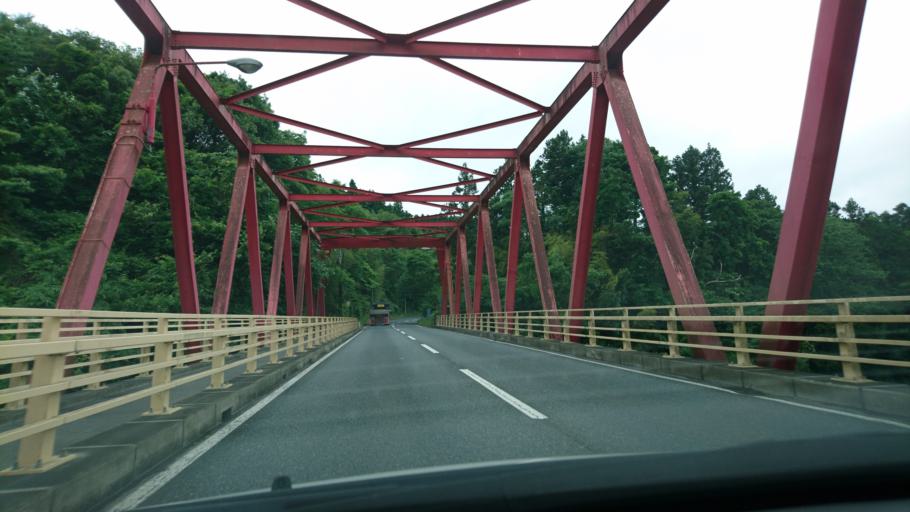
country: JP
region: Iwate
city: Ichinoseki
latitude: 38.9485
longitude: 141.1811
